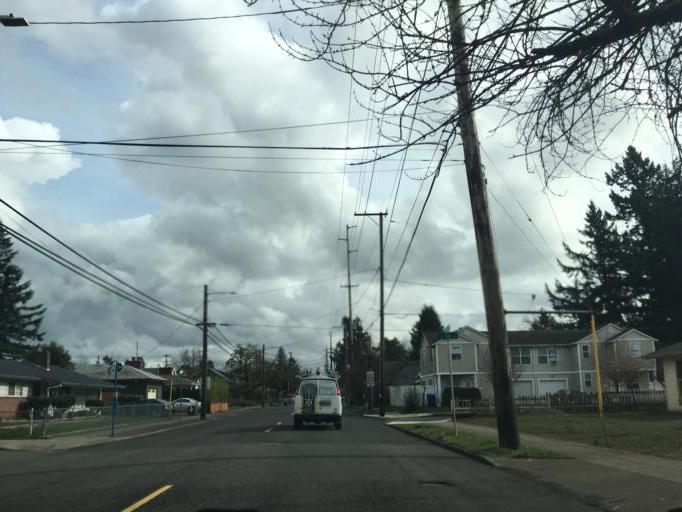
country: US
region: Oregon
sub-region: Multnomah County
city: Lents
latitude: 45.4903
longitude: -122.5850
